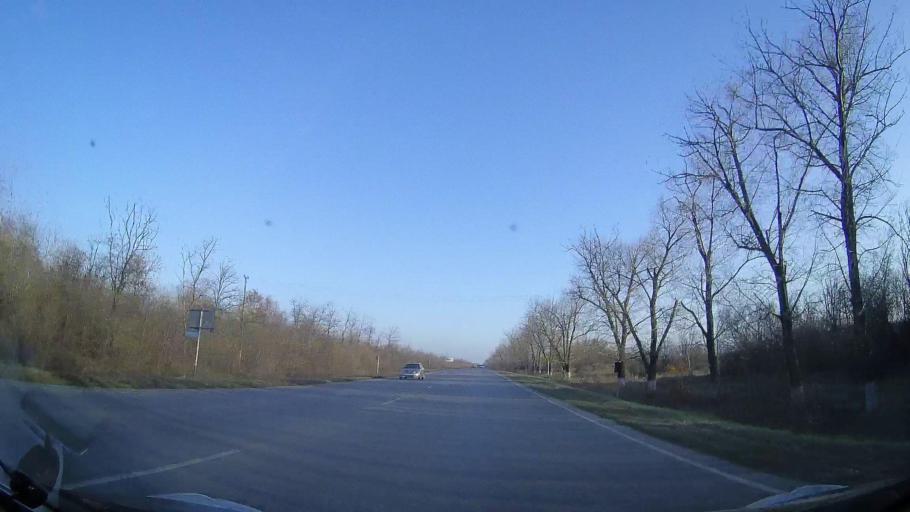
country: RU
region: Rostov
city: Bataysk
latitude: 47.0628
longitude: 39.8120
